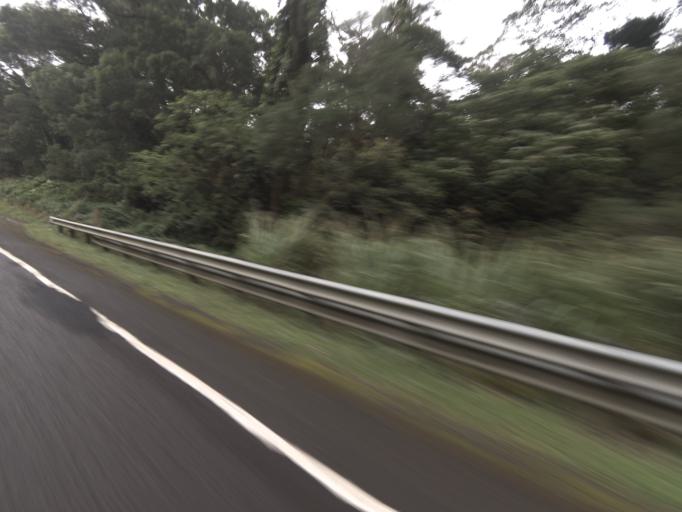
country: US
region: Hawaii
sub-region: Honolulu County
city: Kane'ohe
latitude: 21.3730
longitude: -157.8252
